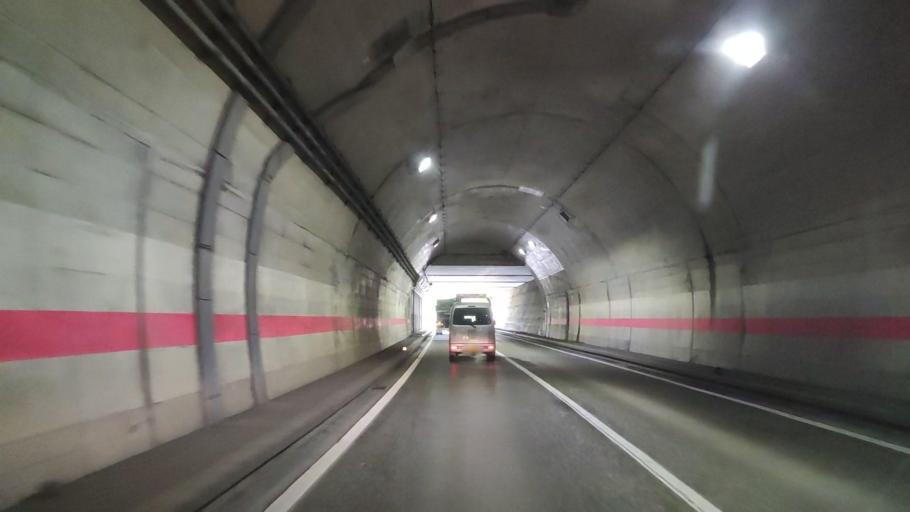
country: JP
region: Gifu
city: Takayama
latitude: 36.2566
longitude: 137.4724
